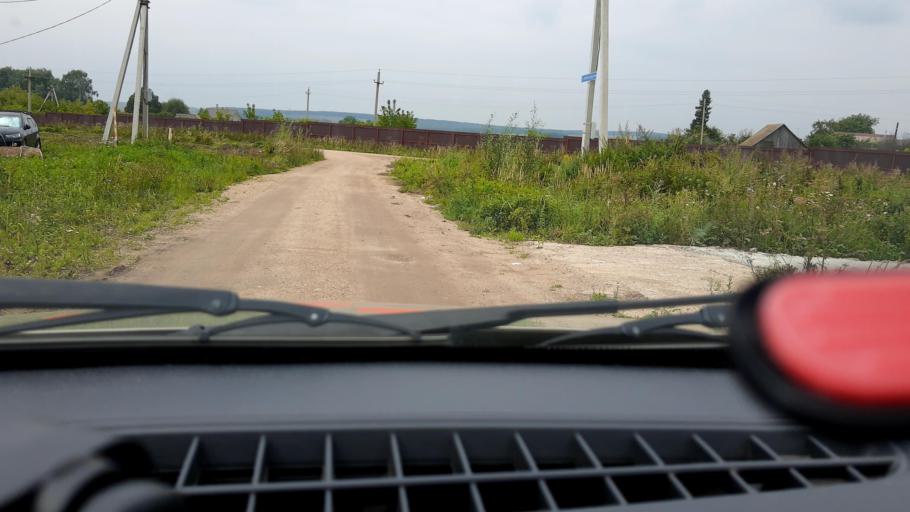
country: RU
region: Bashkortostan
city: Kabakovo
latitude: 54.5801
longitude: 56.2813
